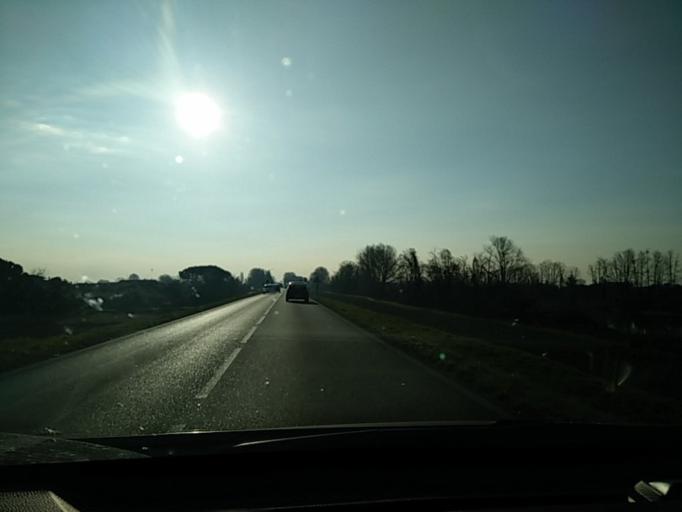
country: IT
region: Veneto
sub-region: Provincia di Venezia
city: Passarella
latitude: 45.5964
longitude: 12.6196
